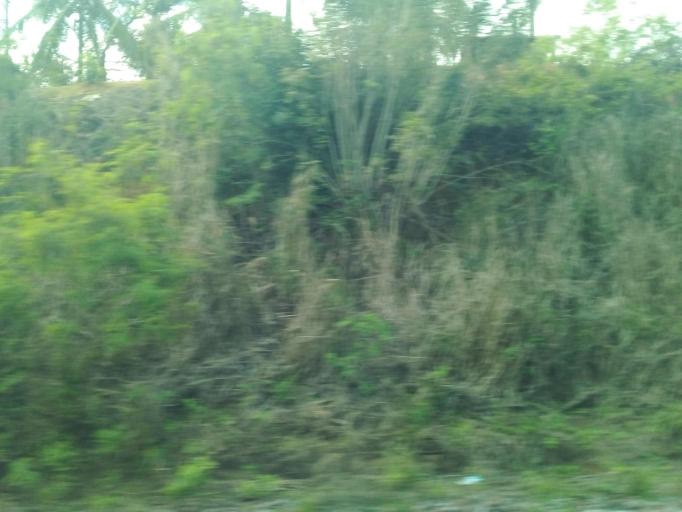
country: BR
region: Minas Gerais
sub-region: Governador Valadares
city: Governador Valadares
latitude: -18.9146
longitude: -42.0061
